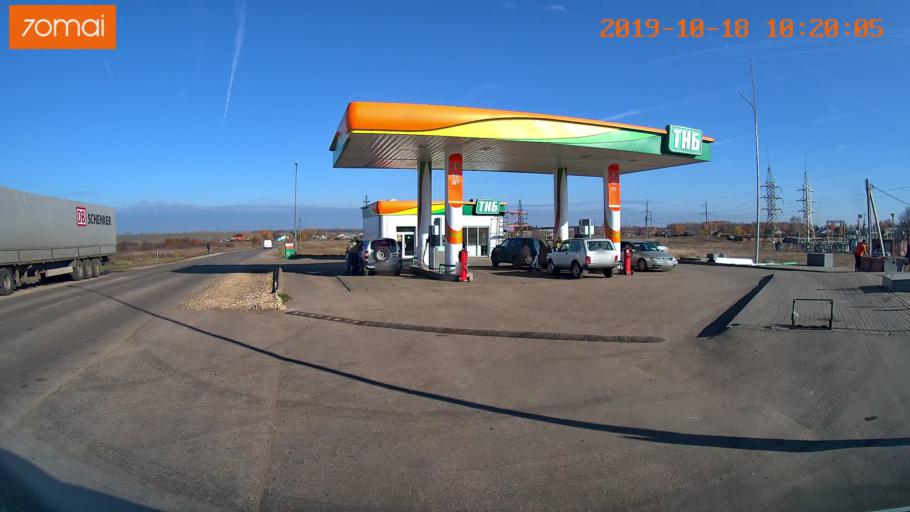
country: RU
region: Tula
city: Kurkino
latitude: 53.4261
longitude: 38.6448
